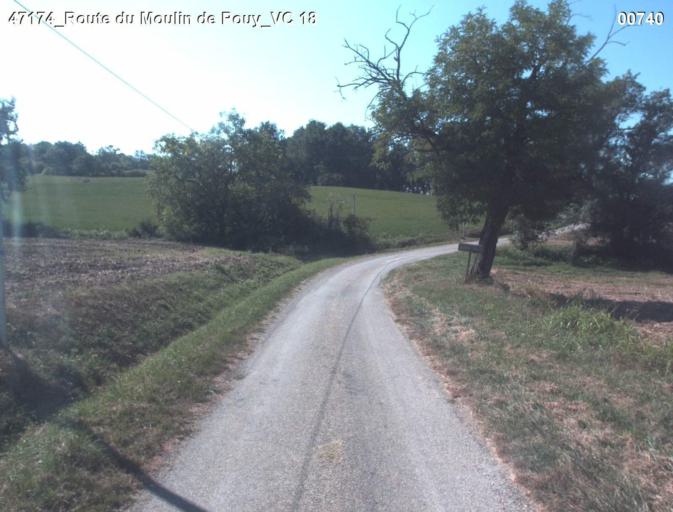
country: FR
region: Aquitaine
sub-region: Departement du Lot-et-Garonne
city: Mezin
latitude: 44.0576
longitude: 0.3188
